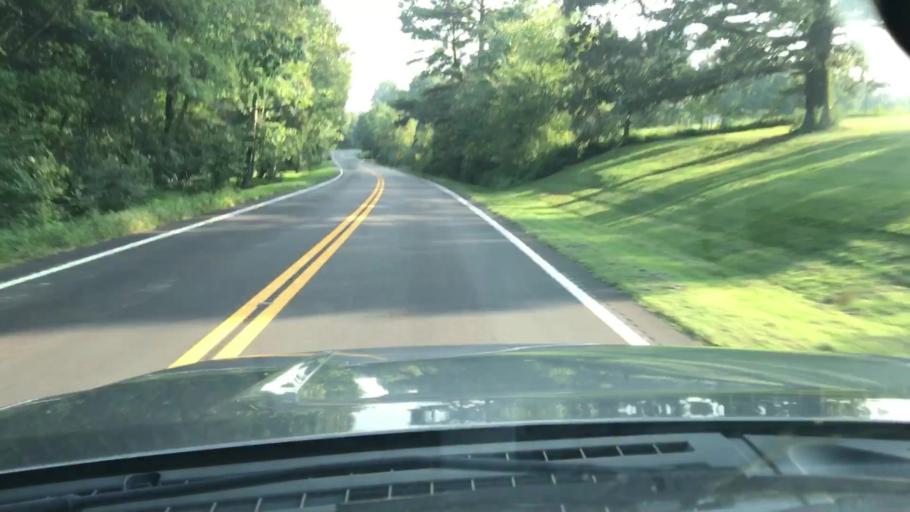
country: US
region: Tennessee
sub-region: Sumner County
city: Portland
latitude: 36.5621
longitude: -86.3880
